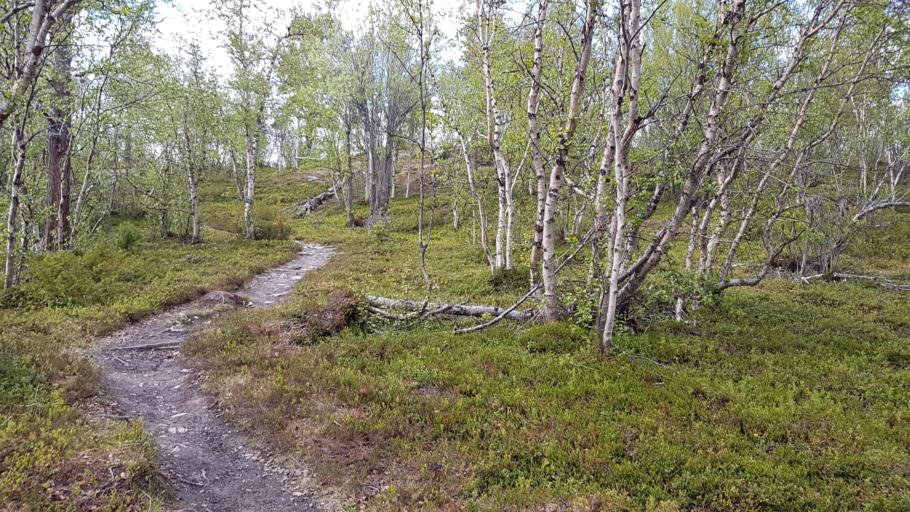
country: NO
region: Troms
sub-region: Bardu
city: Setermoen
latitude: 68.3444
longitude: 18.7773
